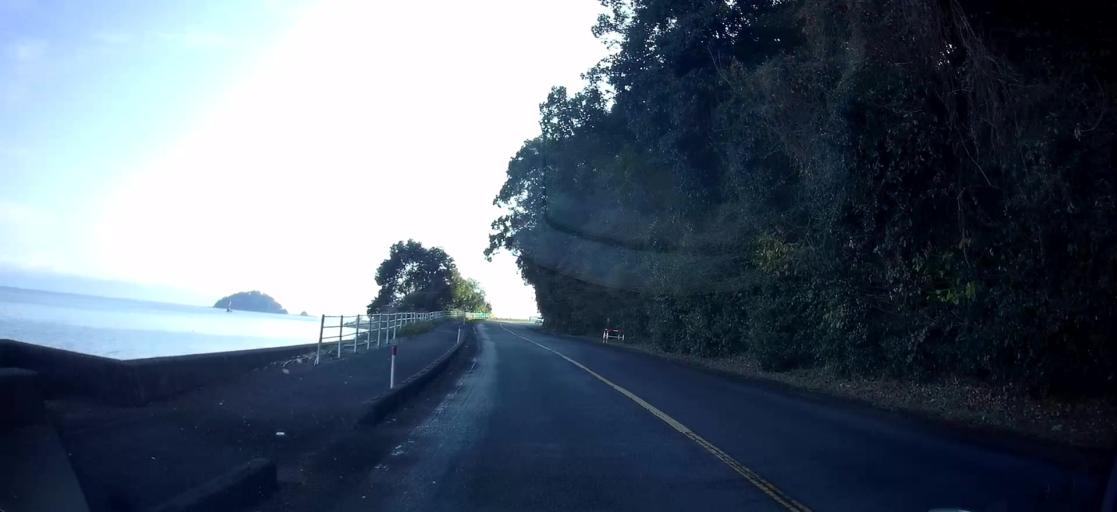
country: JP
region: Kumamoto
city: Yatsushiro
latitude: 32.4781
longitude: 130.4360
